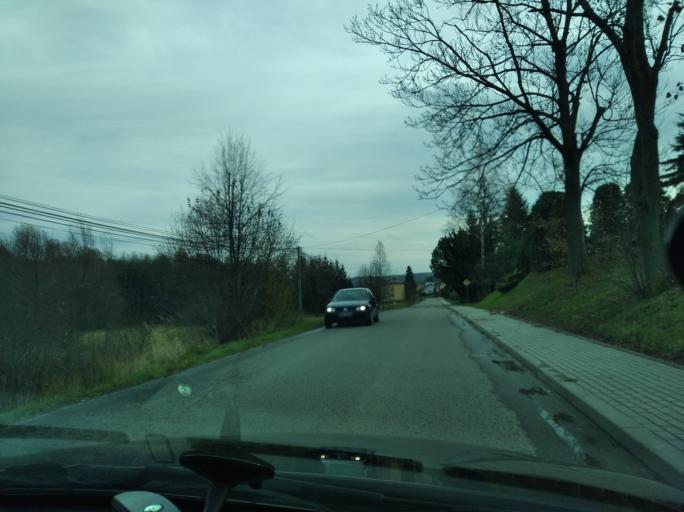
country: PL
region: Subcarpathian Voivodeship
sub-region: Powiat strzyzowski
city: Strzyzow
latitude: 49.9380
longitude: 21.7574
